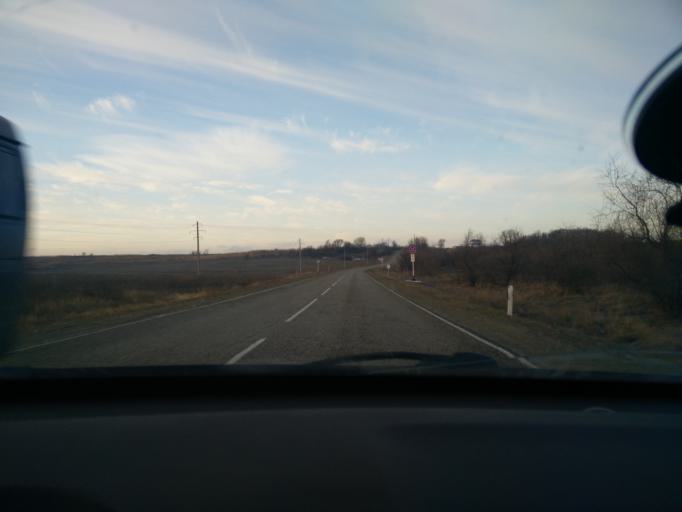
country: RU
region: Stavropol'skiy
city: Balakhonovskoye
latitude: 44.9836
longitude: 41.6960
